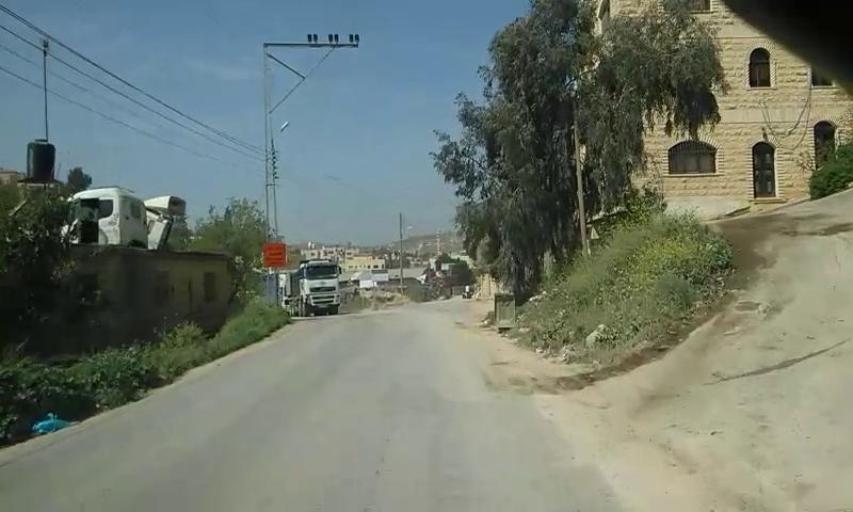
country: PS
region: West Bank
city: Qabatiyah
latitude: 32.4055
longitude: 35.2898
